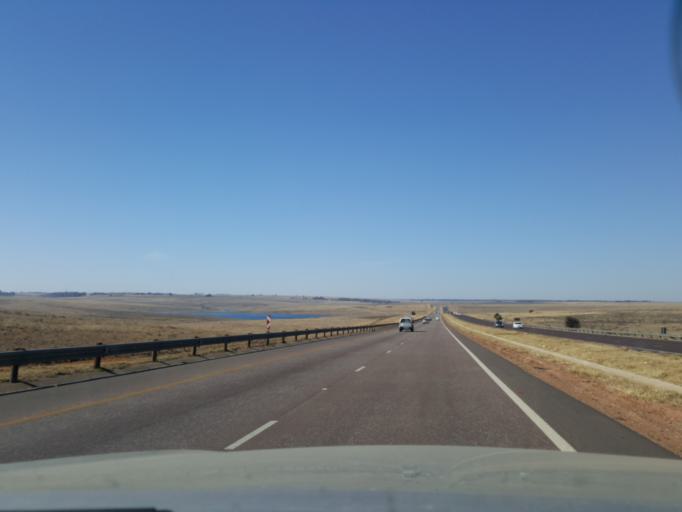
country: ZA
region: Mpumalanga
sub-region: Nkangala District Municipality
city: Middelburg
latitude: -25.8244
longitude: 29.5614
